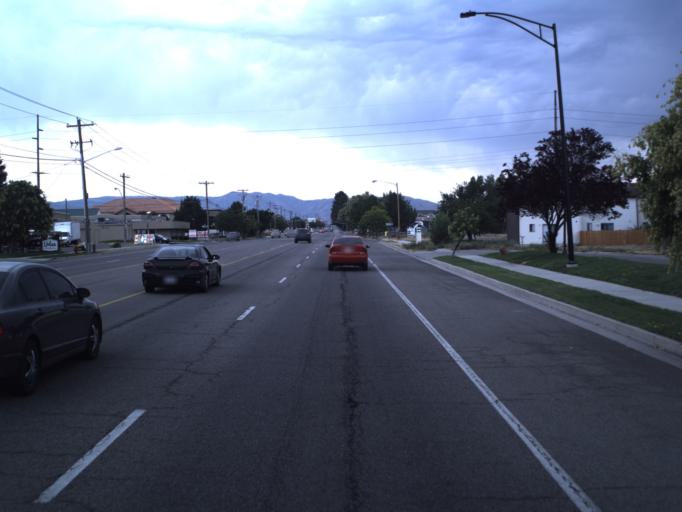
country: US
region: Utah
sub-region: Salt Lake County
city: Sandy City
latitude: 40.5929
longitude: -111.8723
